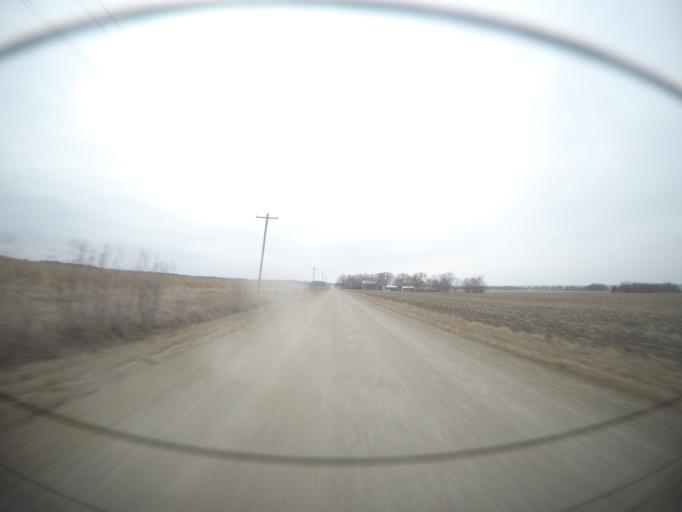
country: US
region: Kansas
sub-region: Pottawatomie County
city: Wamego
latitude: 39.1522
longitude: -96.2967
